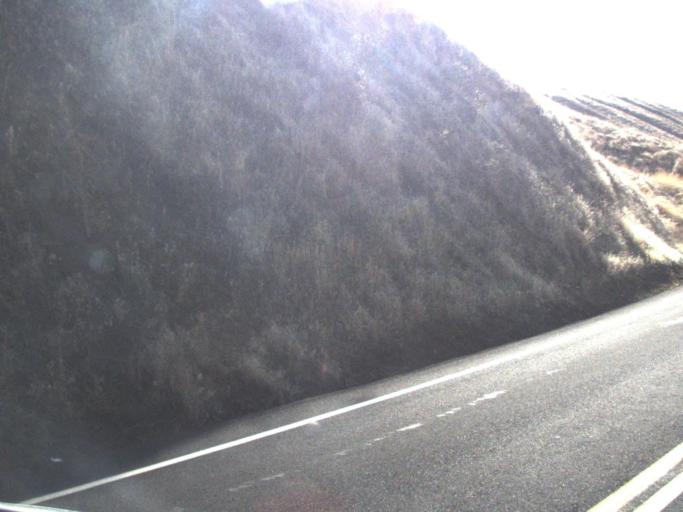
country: US
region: Washington
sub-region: Whitman County
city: Colfax
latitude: 46.7153
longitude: -117.4660
